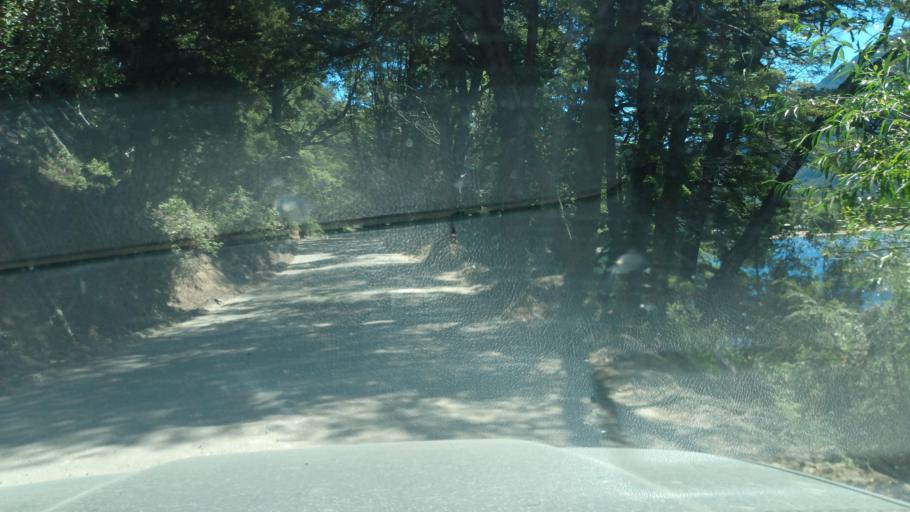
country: AR
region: Neuquen
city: Villa La Angostura
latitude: -40.6165
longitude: -71.5433
